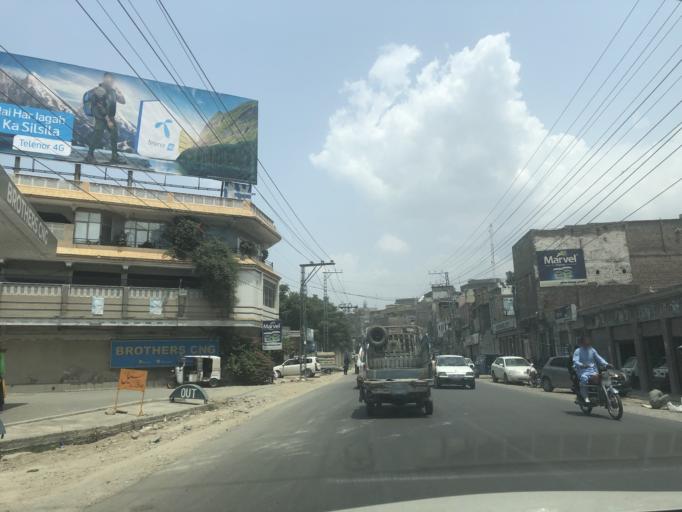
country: PK
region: Khyber Pakhtunkhwa
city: Mingora
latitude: 34.7712
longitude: 72.3460
